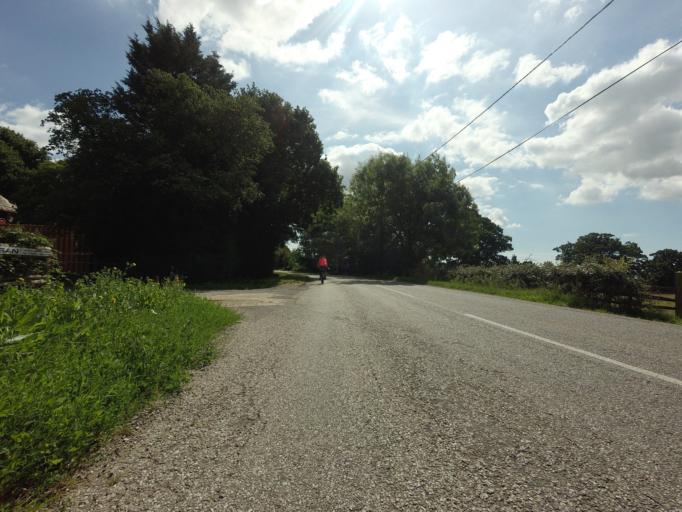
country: GB
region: England
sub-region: Kent
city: Tenterden
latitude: 51.0719
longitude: 0.7423
